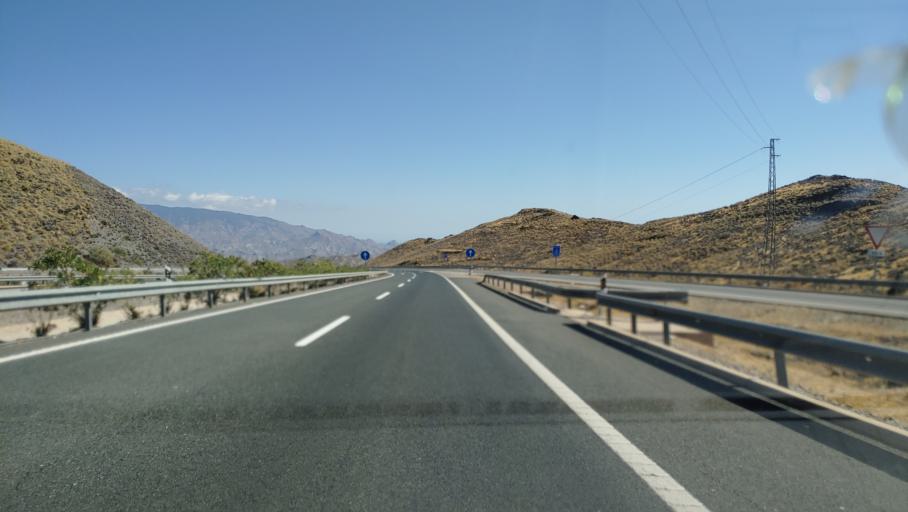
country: ES
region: Andalusia
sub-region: Provincia de Almeria
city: Gergal
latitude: 37.0903
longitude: -2.5230
